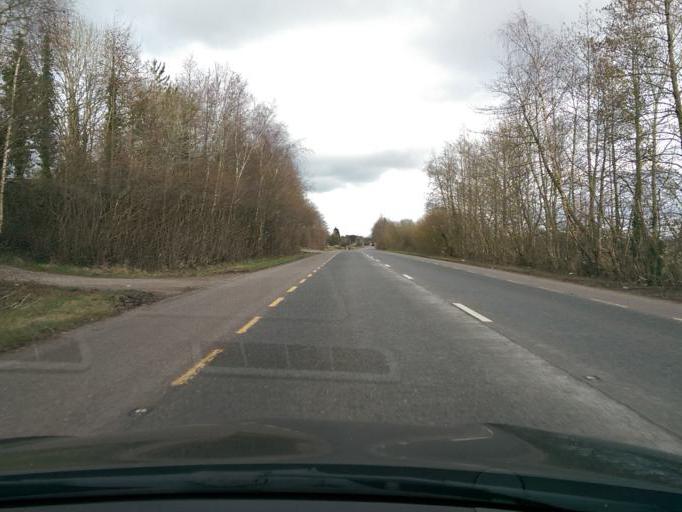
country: IE
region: Leinster
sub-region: An Iarmhi
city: Moate
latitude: 53.3916
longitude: -7.7610
